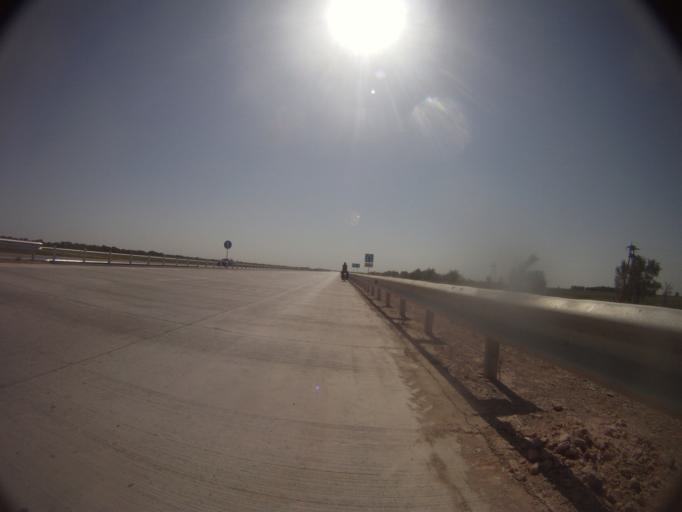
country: KZ
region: Ongtustik Qazaqstan
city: Turkestan
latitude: 43.1640
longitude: 68.5302
